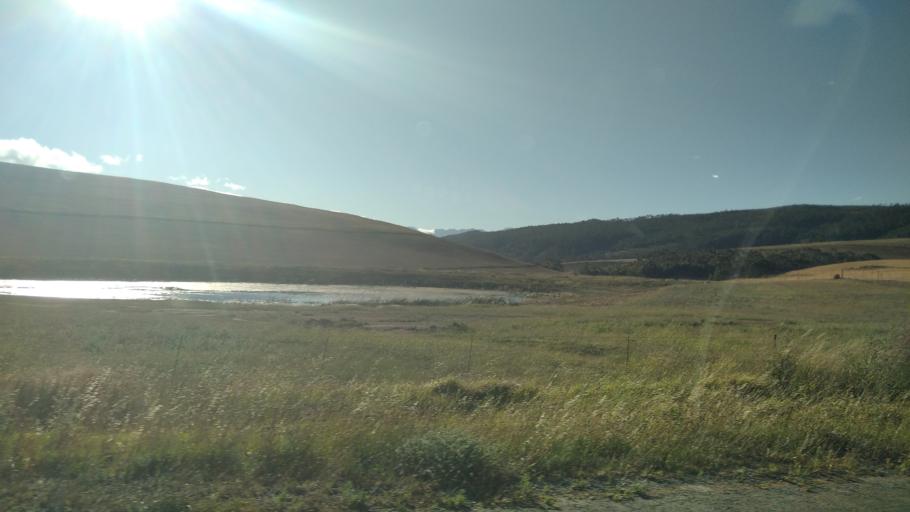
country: ZA
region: Western Cape
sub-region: Overberg District Municipality
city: Caledon
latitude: -34.1204
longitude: 19.2989
